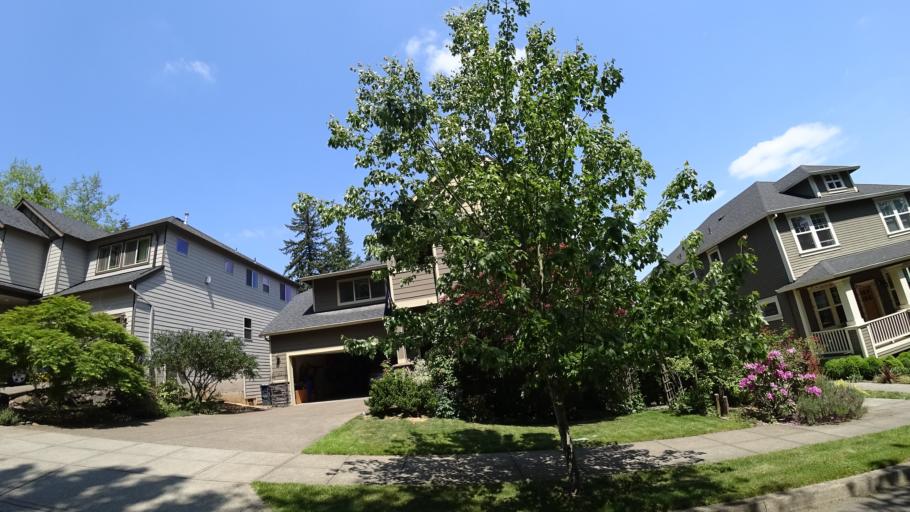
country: US
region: Oregon
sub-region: Washington County
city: Metzger
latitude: 45.4404
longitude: -122.7183
